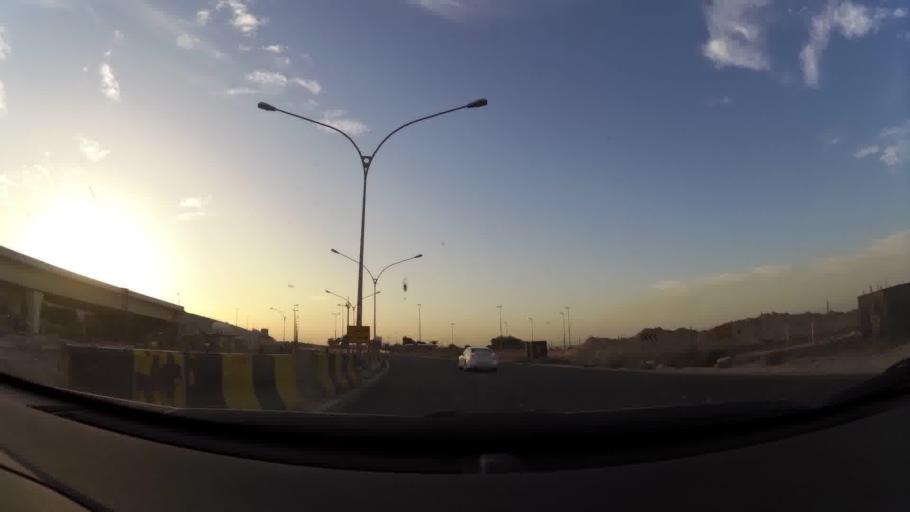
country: KW
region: Al Asimah
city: Ar Rabiyah
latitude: 29.3185
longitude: 47.8629
